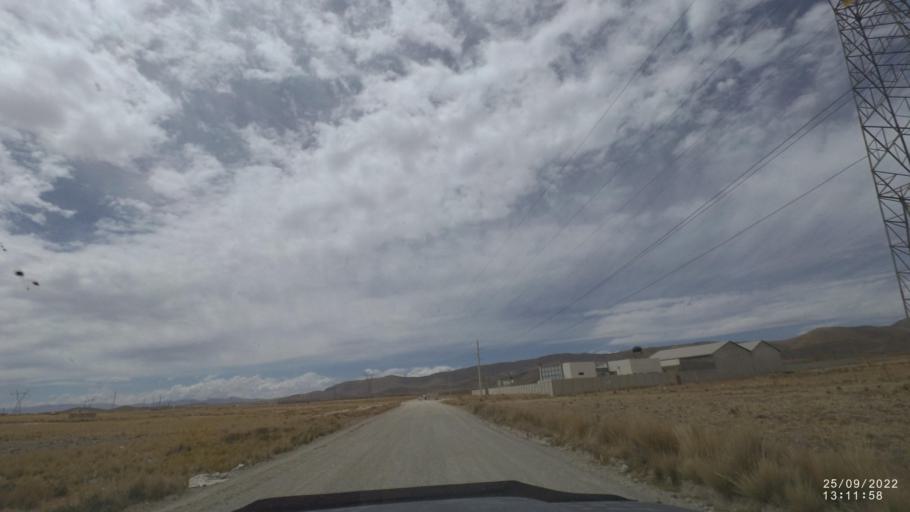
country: BO
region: Oruro
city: Oruro
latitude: -17.9606
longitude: -67.0430
